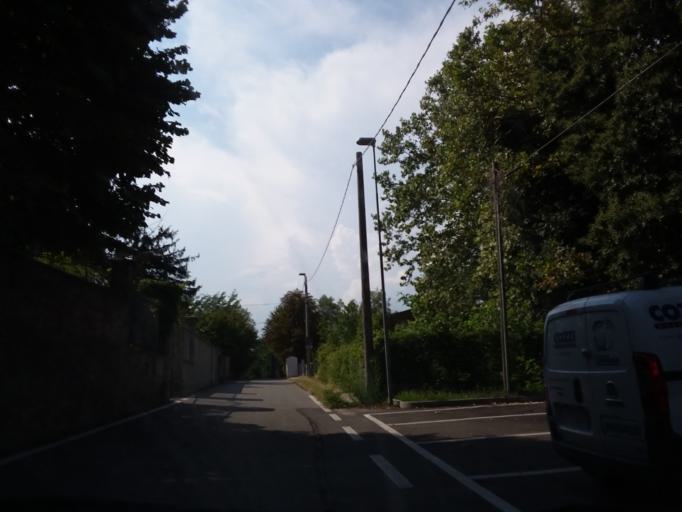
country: IT
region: Piedmont
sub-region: Provincia di Torino
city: Pianezza
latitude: 45.0857
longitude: 7.5456
